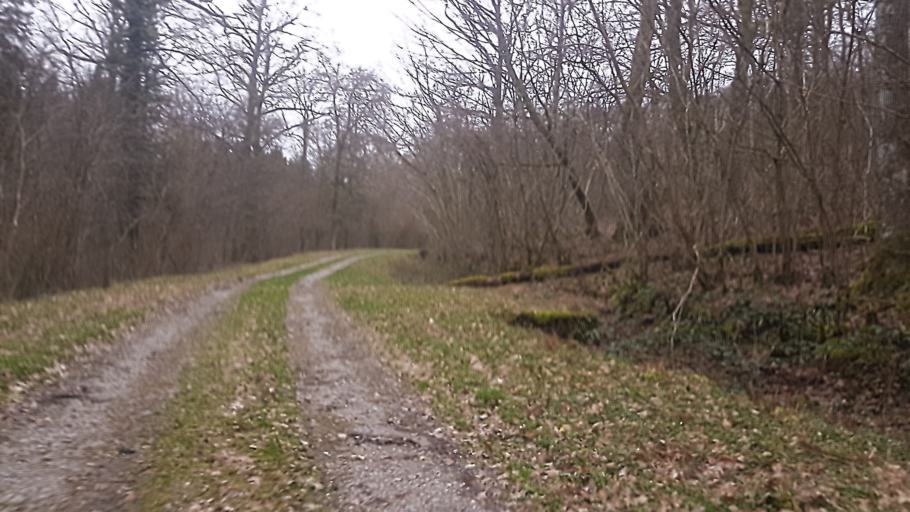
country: FR
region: Champagne-Ardenne
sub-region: Departement des Ardennes
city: Haybes
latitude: 50.0472
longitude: 4.6219
